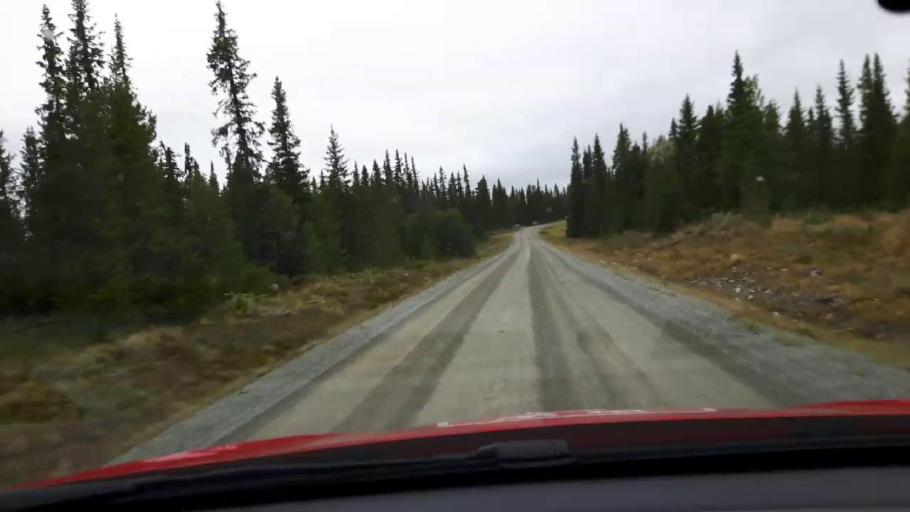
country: SE
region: Jaemtland
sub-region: Bergs Kommun
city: Hoverberg
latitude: 62.8727
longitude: 13.9659
